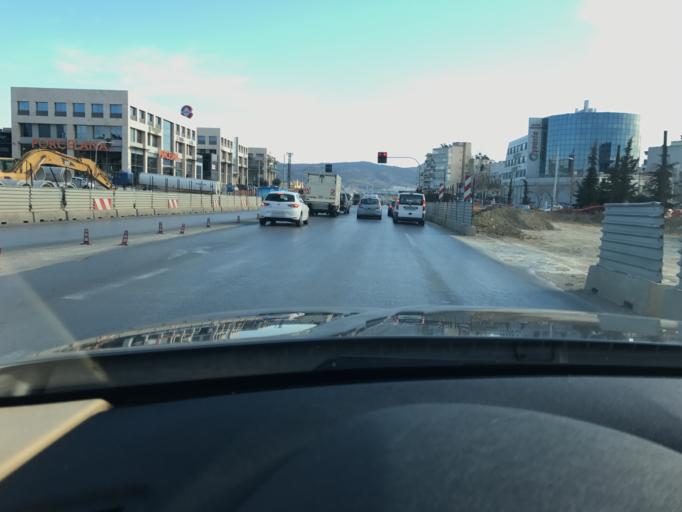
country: GR
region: Central Macedonia
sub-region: Nomos Thessalonikis
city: Stavroupoli
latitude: 40.6773
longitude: 22.9243
